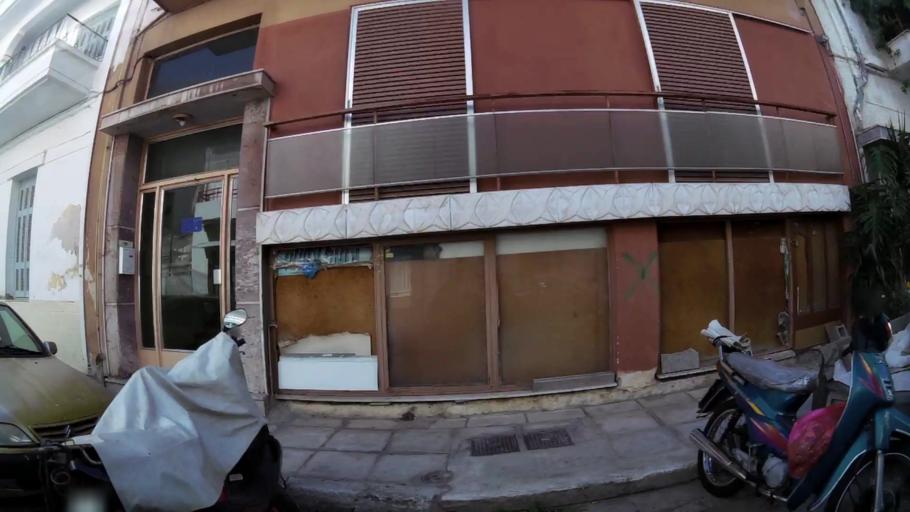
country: GR
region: Attica
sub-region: Nomos Piraios
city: Drapetsona
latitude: 37.9571
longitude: 23.6290
